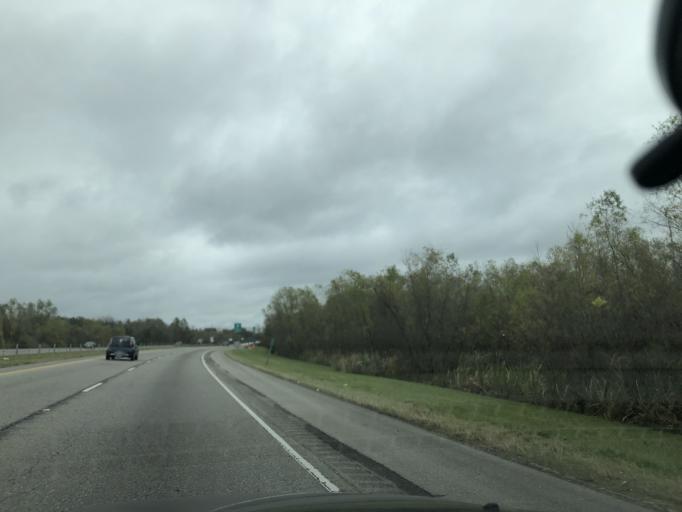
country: US
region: Louisiana
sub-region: Saint Charles Parish
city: Destrehan
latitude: 29.9626
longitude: -90.3590
